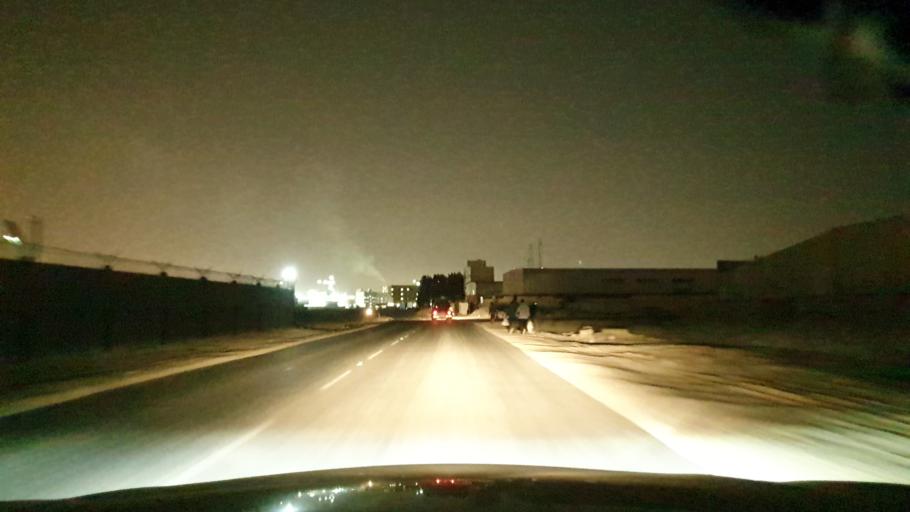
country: BH
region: Northern
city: Sitrah
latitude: 26.0906
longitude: 50.6160
